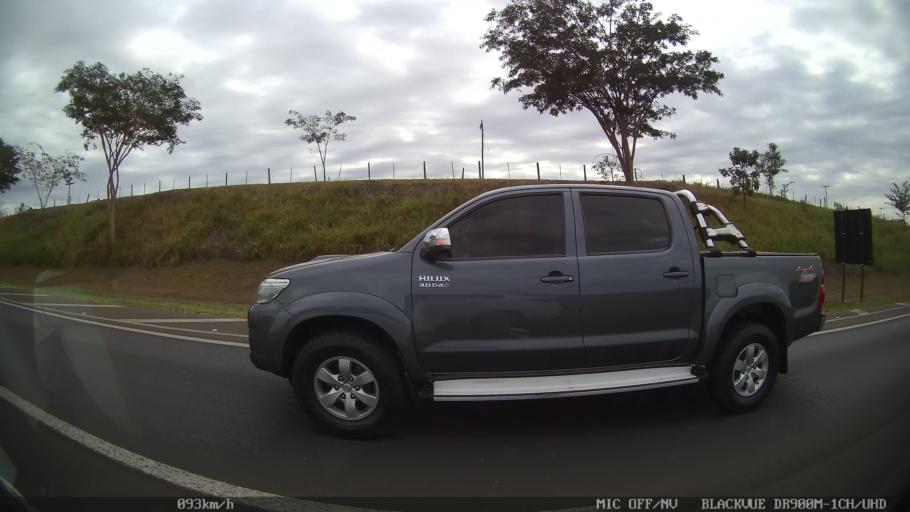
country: BR
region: Sao Paulo
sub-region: Sao Jose Do Rio Preto
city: Sao Jose do Rio Preto
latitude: -20.8142
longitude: -49.4718
